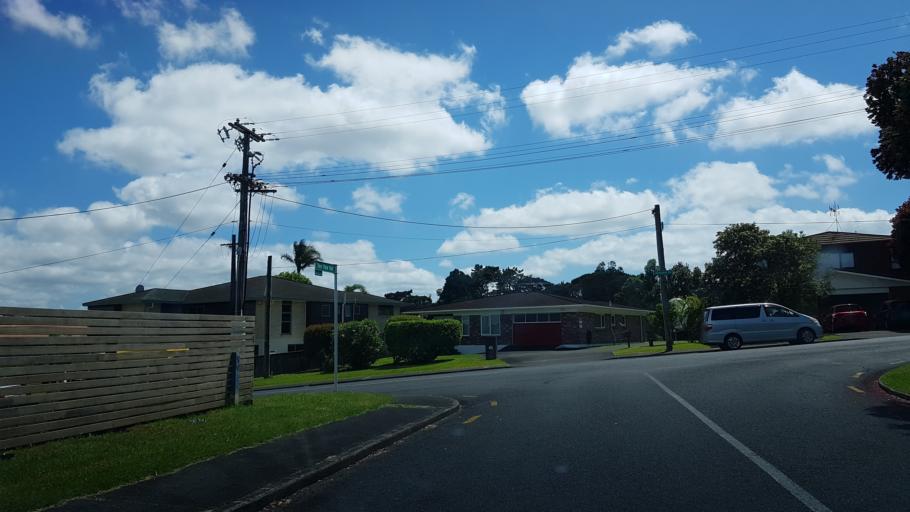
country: NZ
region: Auckland
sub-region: Auckland
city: North Shore
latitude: -36.7882
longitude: 174.7097
